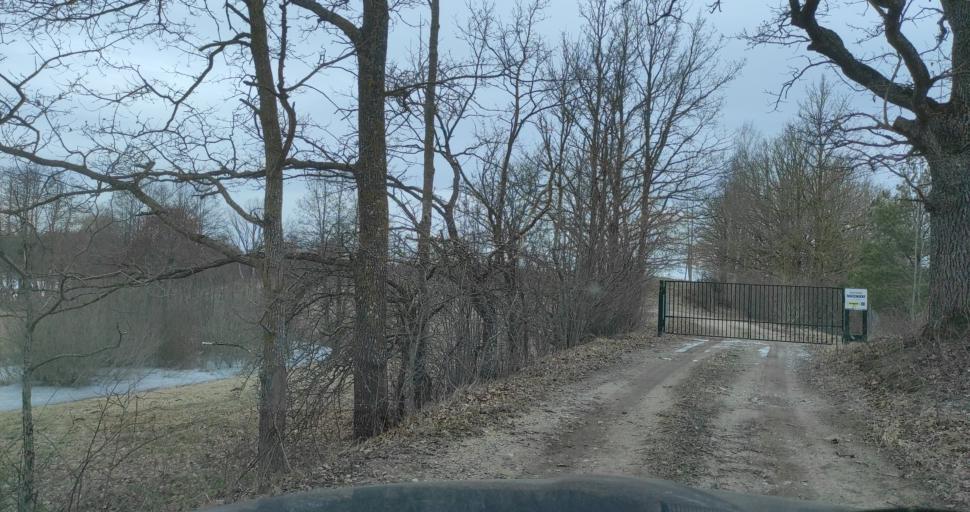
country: LV
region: Tukuma Rajons
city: Tukums
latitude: 57.0963
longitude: 23.0936
